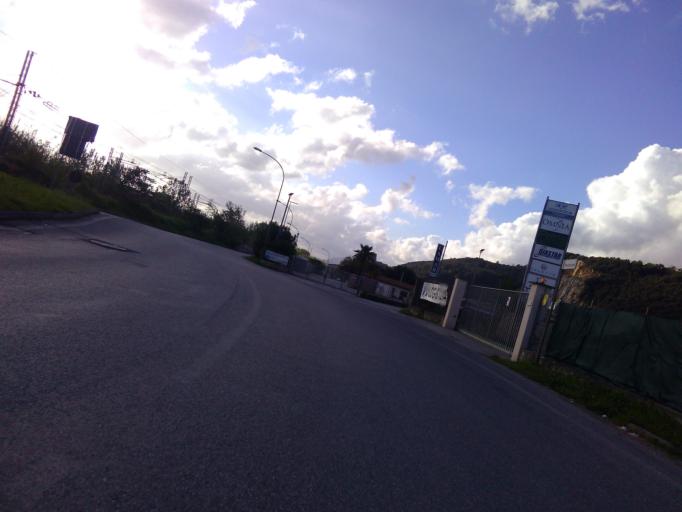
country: IT
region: Tuscany
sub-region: Provincia di Lucca
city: Strettoia
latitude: 43.9899
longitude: 10.1833
